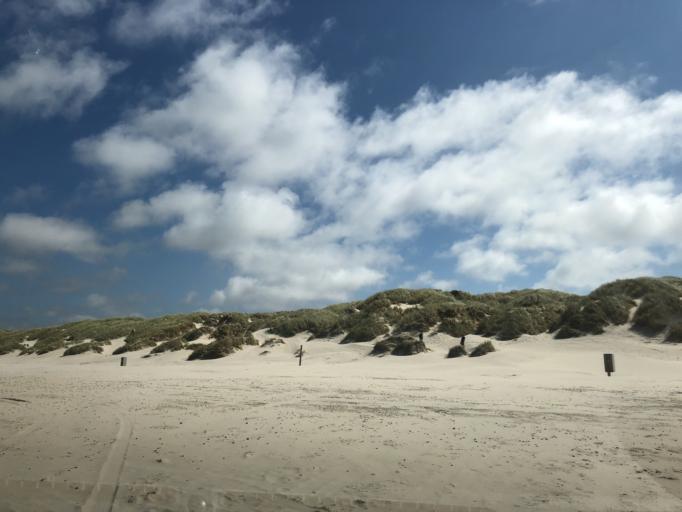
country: DK
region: North Denmark
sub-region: Jammerbugt Kommune
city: Pandrup
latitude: 57.2574
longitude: 9.5820
